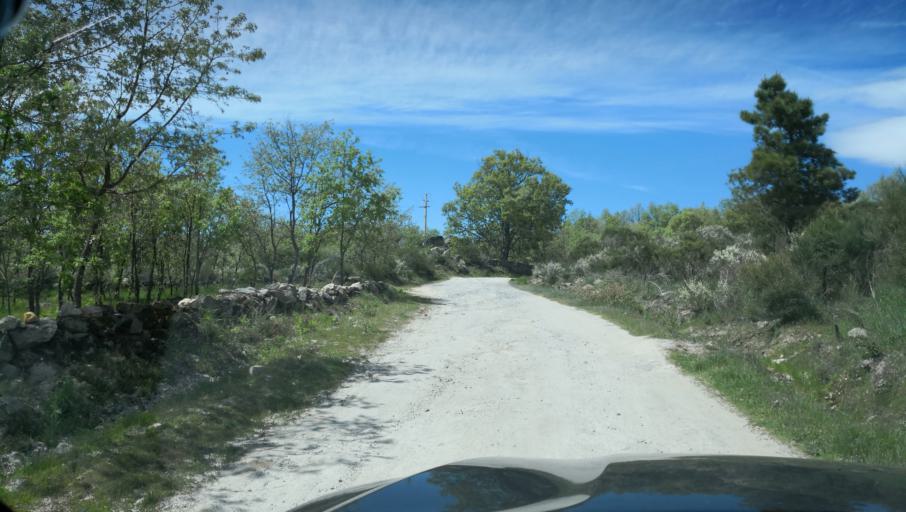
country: PT
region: Vila Real
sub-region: Vila Real
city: Vila Real
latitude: 41.3744
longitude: -7.6777
